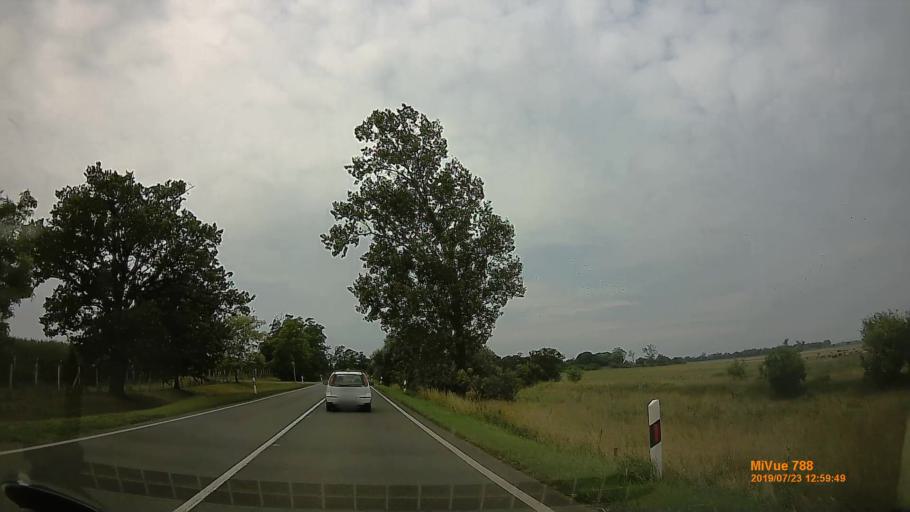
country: HU
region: Szabolcs-Szatmar-Bereg
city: Tiszalok
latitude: 47.9582
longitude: 21.4304
